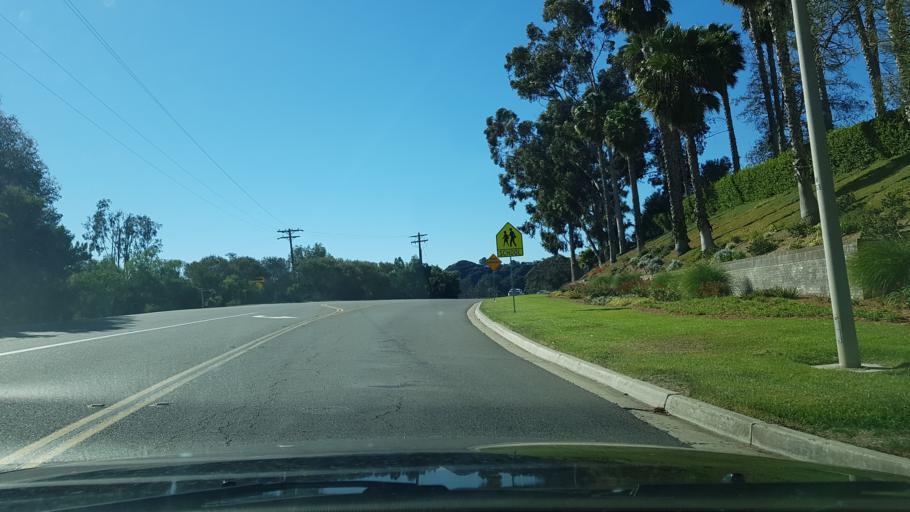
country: US
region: California
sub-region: San Diego County
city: Solana Beach
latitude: 33.0224
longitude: -117.2502
